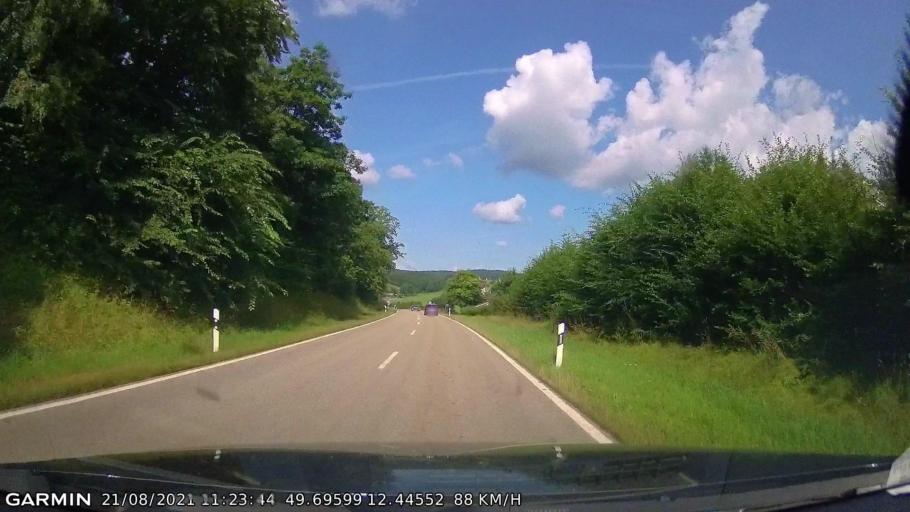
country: DE
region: Bavaria
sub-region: Upper Palatinate
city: Georgenberg
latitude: 49.6961
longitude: 12.4454
